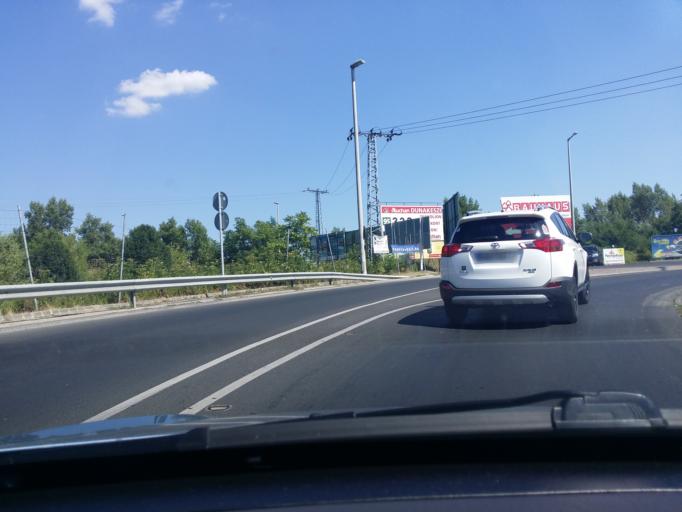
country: HU
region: Pest
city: Dunakeszi
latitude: 47.6055
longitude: 19.1228
